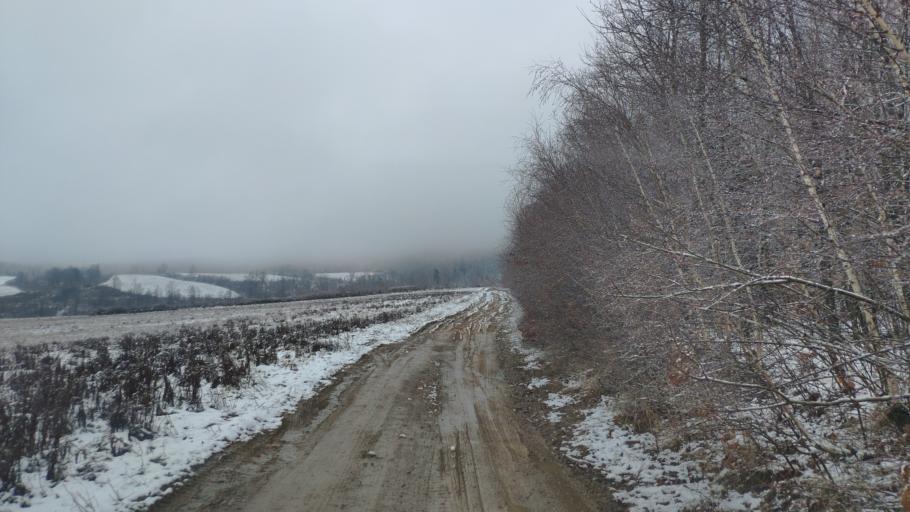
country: SK
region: Kosicky
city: Moldava nad Bodvou
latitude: 48.7395
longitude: 21.0873
